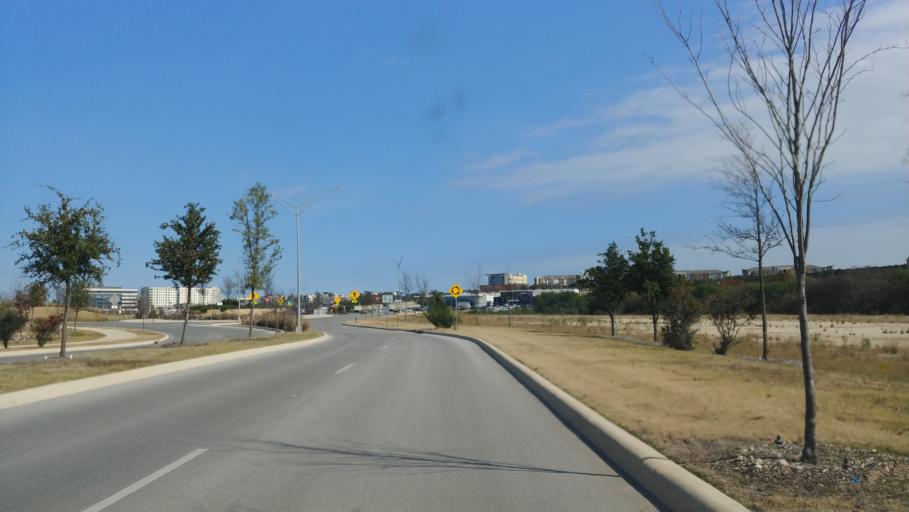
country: US
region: Texas
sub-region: Bexar County
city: Shavano Park
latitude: 29.5807
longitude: -98.6007
